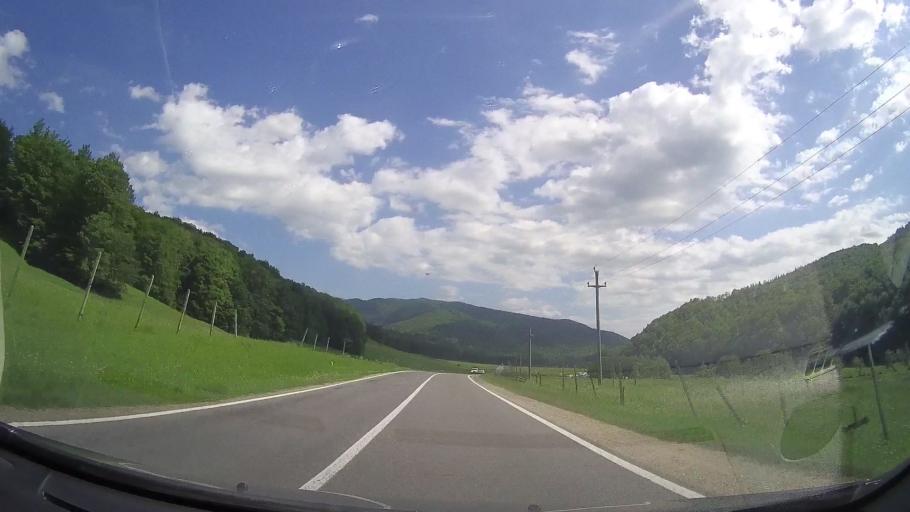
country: RO
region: Prahova
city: Maneciu
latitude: 45.4290
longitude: 25.9395
